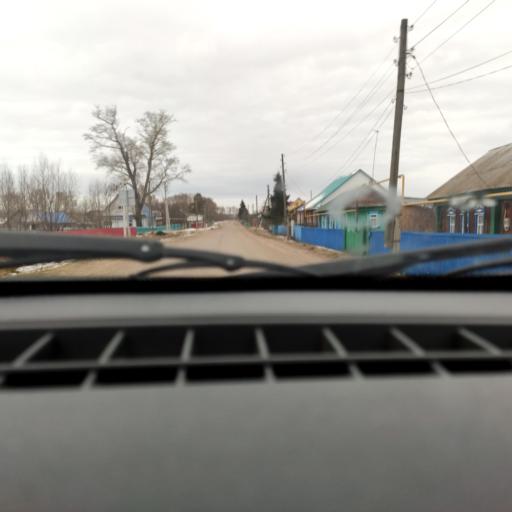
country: RU
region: Bashkortostan
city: Tolbazy
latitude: 54.2552
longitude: 55.9186
